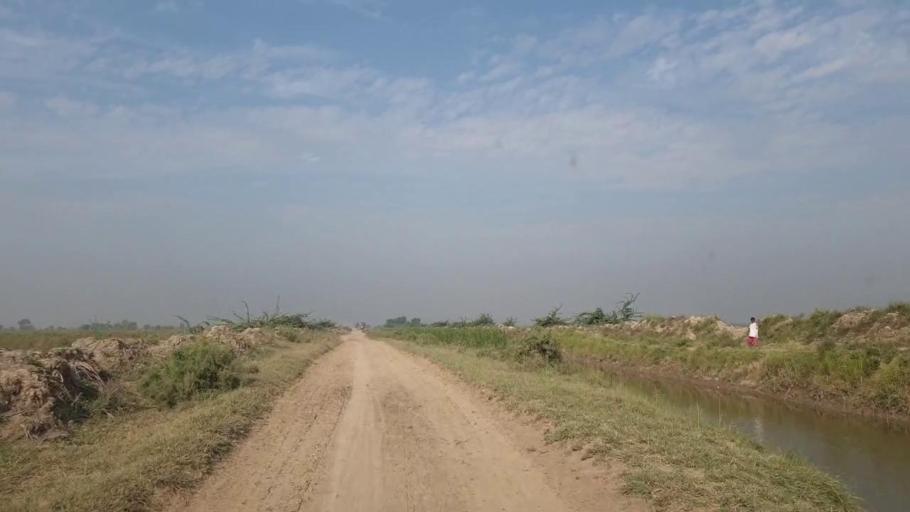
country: PK
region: Sindh
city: Tando Bago
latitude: 24.8730
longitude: 68.9648
